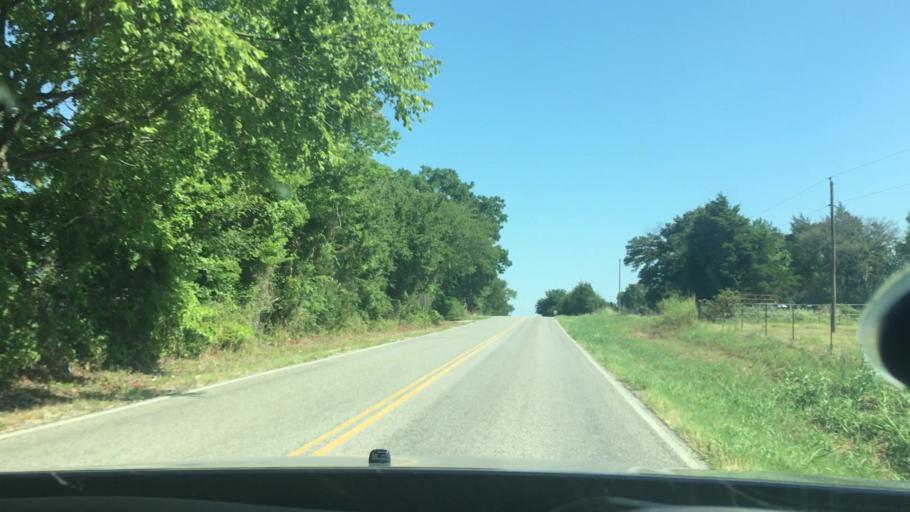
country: US
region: Oklahoma
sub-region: Johnston County
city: Tishomingo
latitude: 34.2583
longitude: -96.6186
